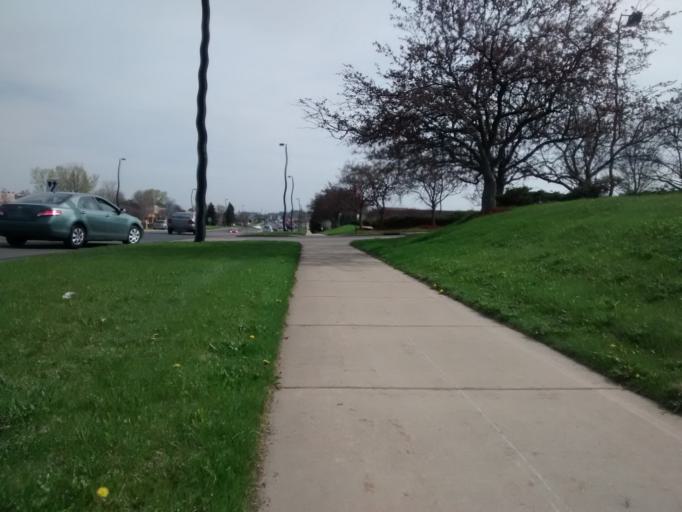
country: US
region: Minnesota
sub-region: Dakota County
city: Burnsville
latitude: 44.7513
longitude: -93.2881
